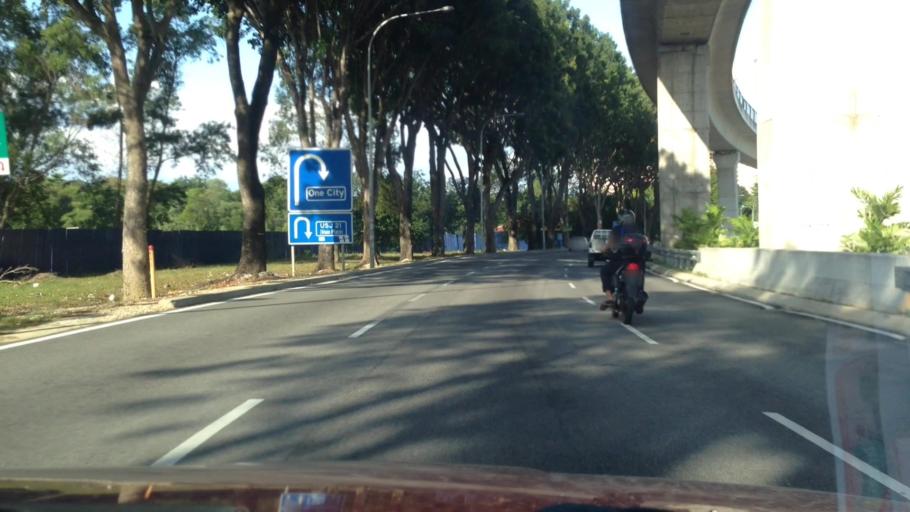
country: MY
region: Selangor
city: Subang Jaya
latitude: 3.0303
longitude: 101.5825
